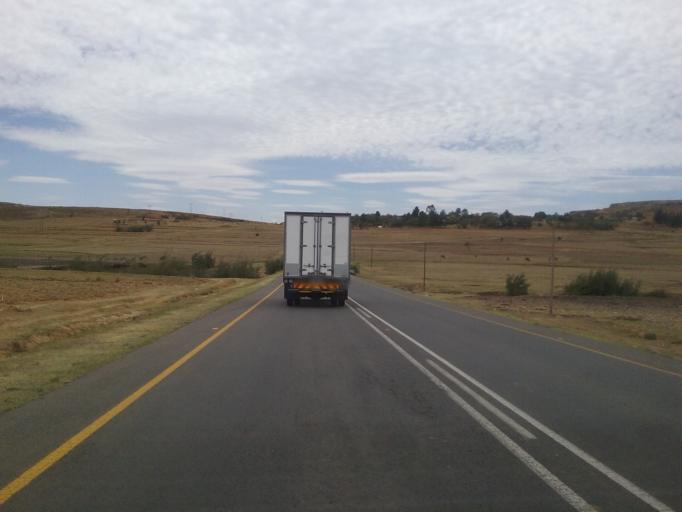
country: LS
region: Maseru
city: Nako
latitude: -29.6386
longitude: 27.4779
